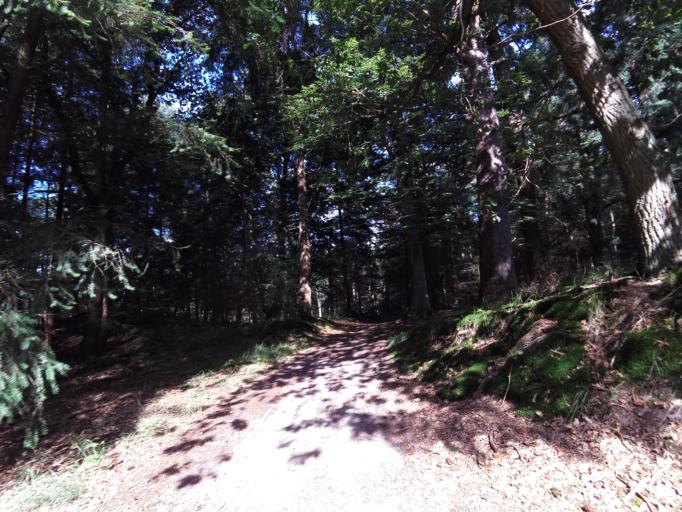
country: NL
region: North Brabant
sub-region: Gemeente Woensdrecht
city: Woensdrecht
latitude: 51.4657
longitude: 4.3649
